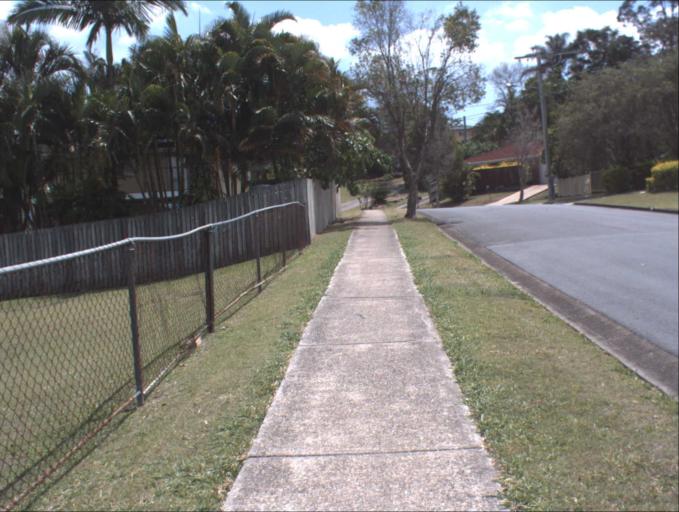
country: AU
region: Queensland
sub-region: Logan
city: Springwood
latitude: -27.6180
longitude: 153.1355
